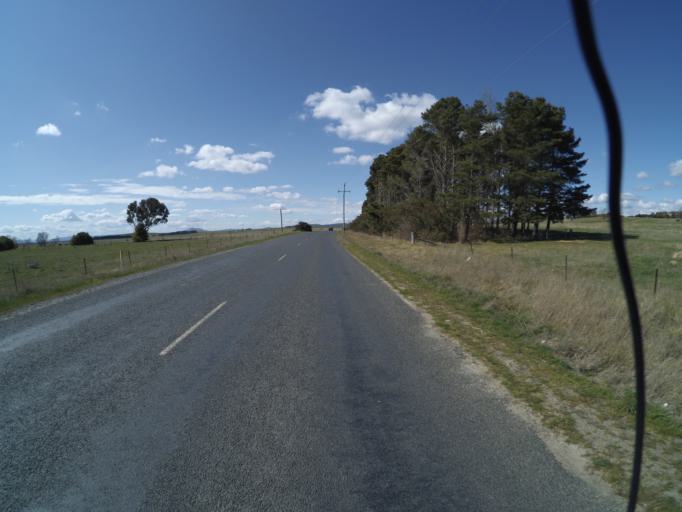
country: AU
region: New South Wales
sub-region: Palerang
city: Bungendore
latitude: -35.2281
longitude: 149.4506
